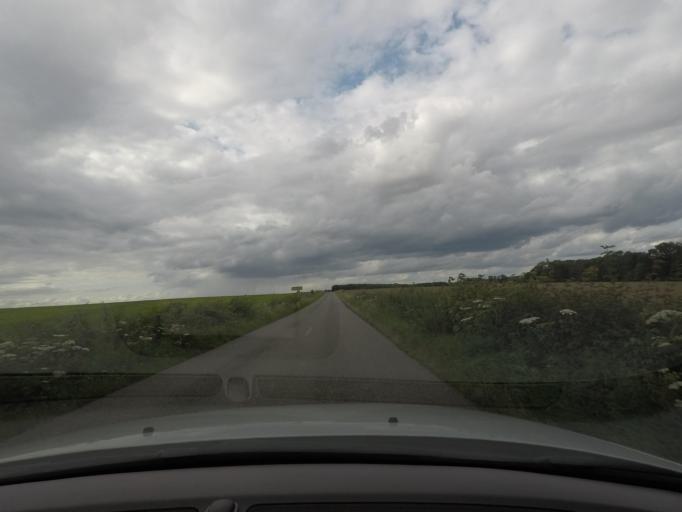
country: FR
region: Haute-Normandie
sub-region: Departement de l'Eure
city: Les Andelys
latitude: 49.2604
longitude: 1.3610
